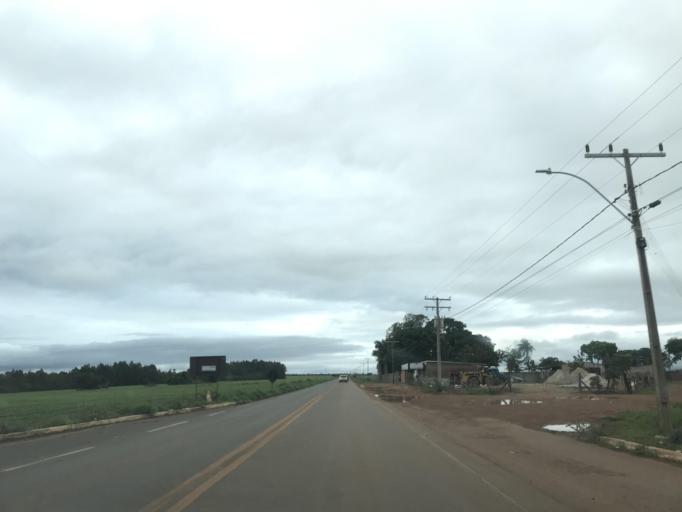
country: BR
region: Goias
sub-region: Luziania
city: Luziania
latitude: -16.3110
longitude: -48.0142
